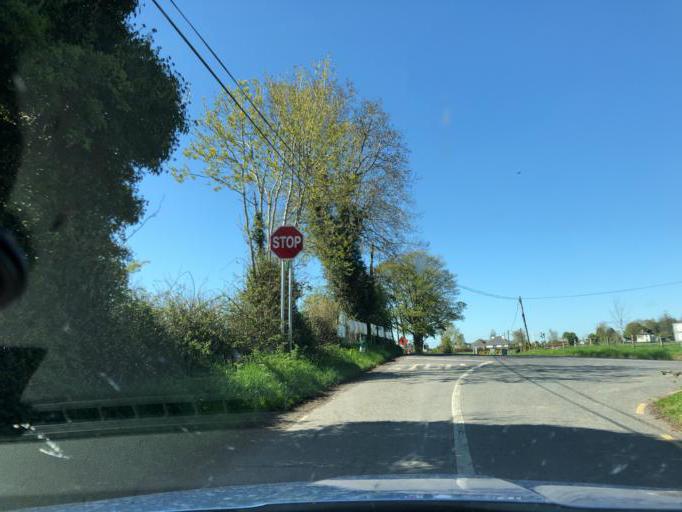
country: IE
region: Connaught
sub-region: County Galway
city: Portumna
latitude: 53.1774
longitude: -8.1972
